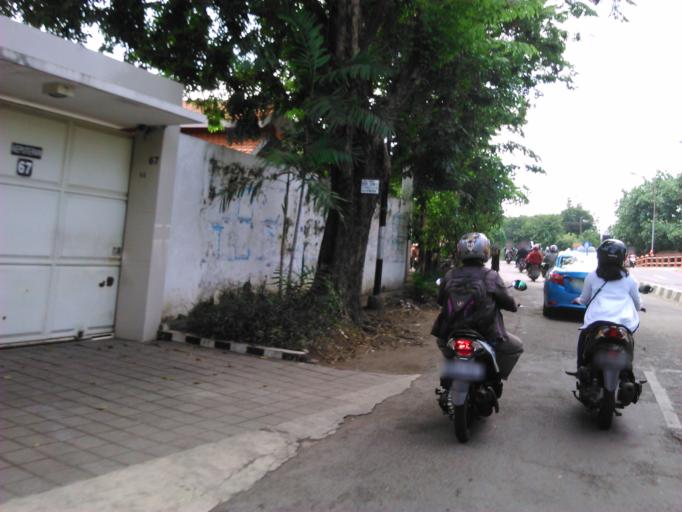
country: ID
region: East Java
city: Gubengairlangga
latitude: -7.2774
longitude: 112.7433
